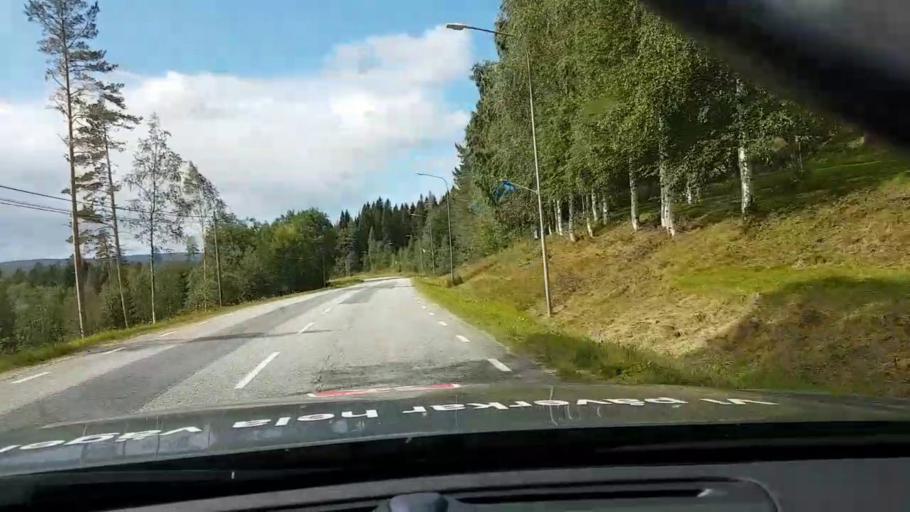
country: SE
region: Vaesterbotten
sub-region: Asele Kommun
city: Asele
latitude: 63.7912
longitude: 17.6239
